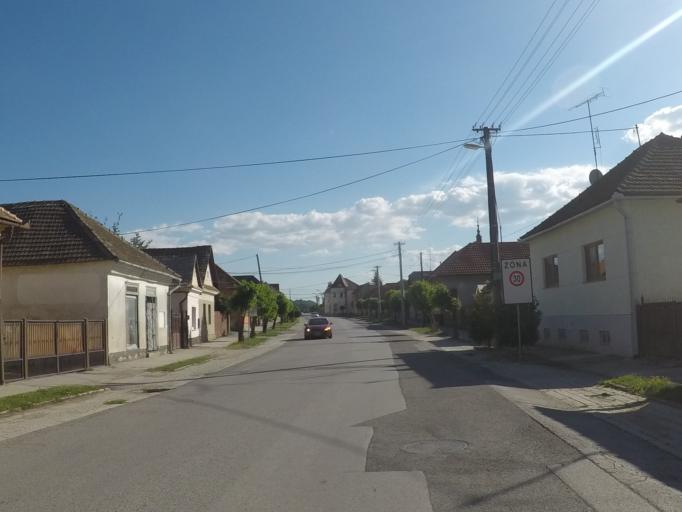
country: SK
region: Kosicky
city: Roznava
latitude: 48.5473
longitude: 20.4047
